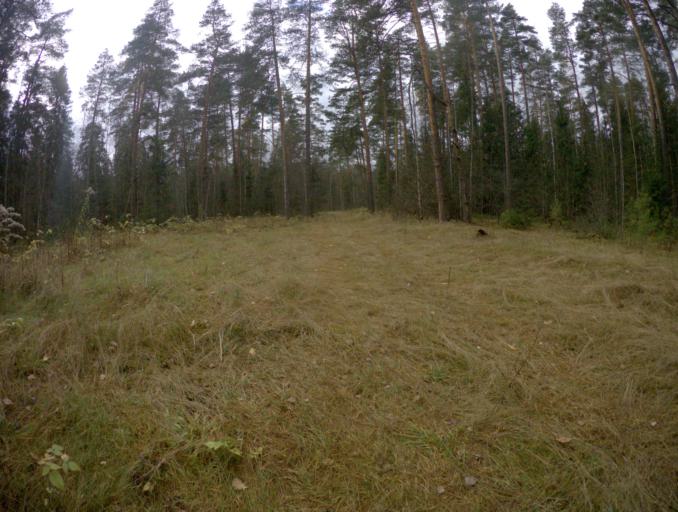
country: RU
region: Vladimir
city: Orgtrud
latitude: 56.1125
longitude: 40.6189
